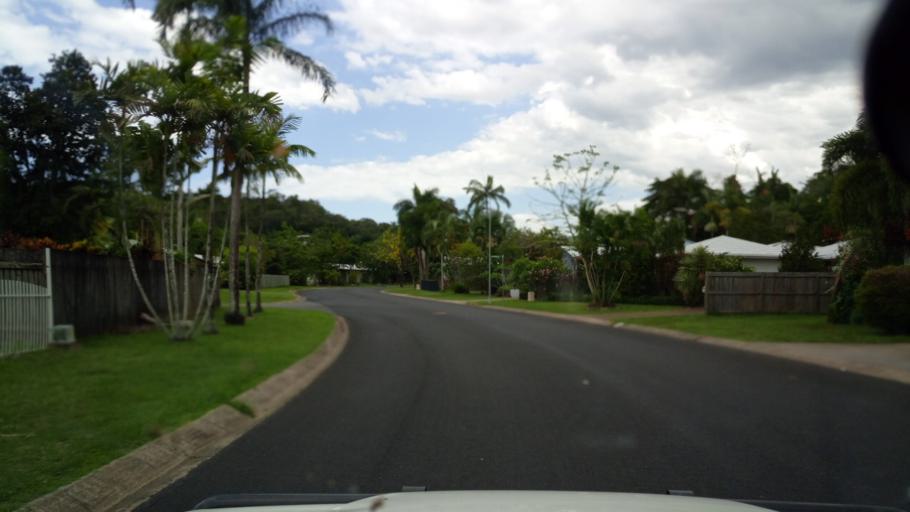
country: AU
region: Queensland
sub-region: Cairns
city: Redlynch
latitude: -16.9055
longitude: 145.7139
